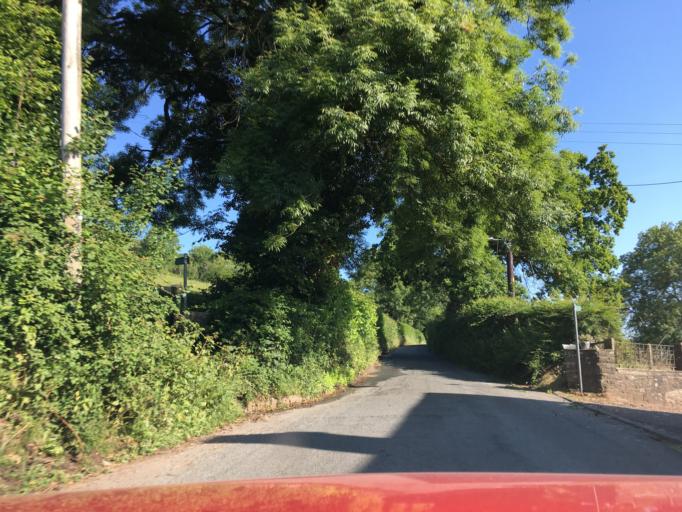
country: GB
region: England
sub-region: Gloucestershire
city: Lydney
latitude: 51.7669
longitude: -2.4834
